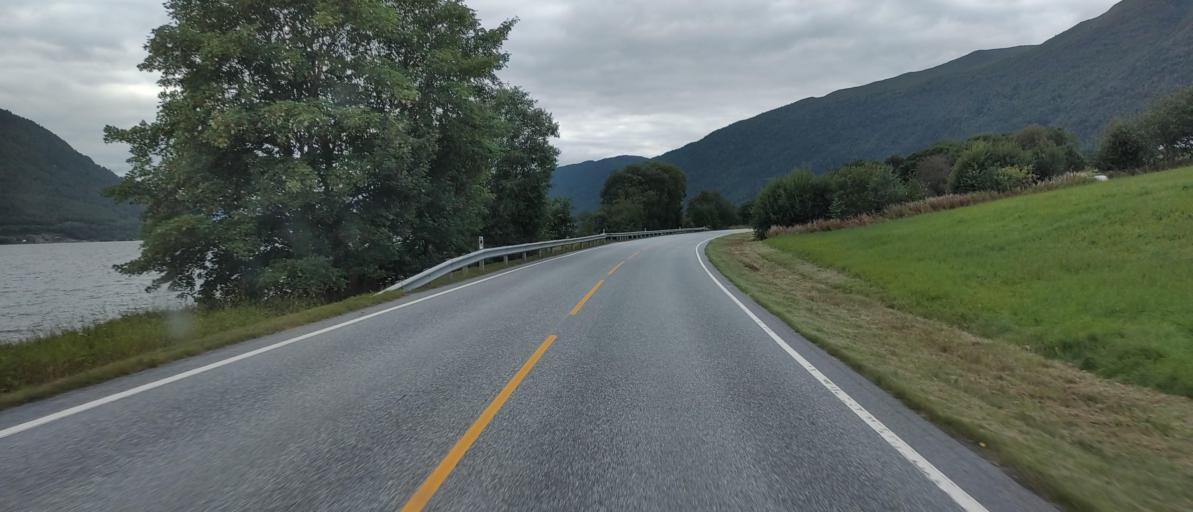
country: NO
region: More og Romsdal
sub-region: Rauma
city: Andalsnes
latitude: 62.5765
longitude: 7.7593
